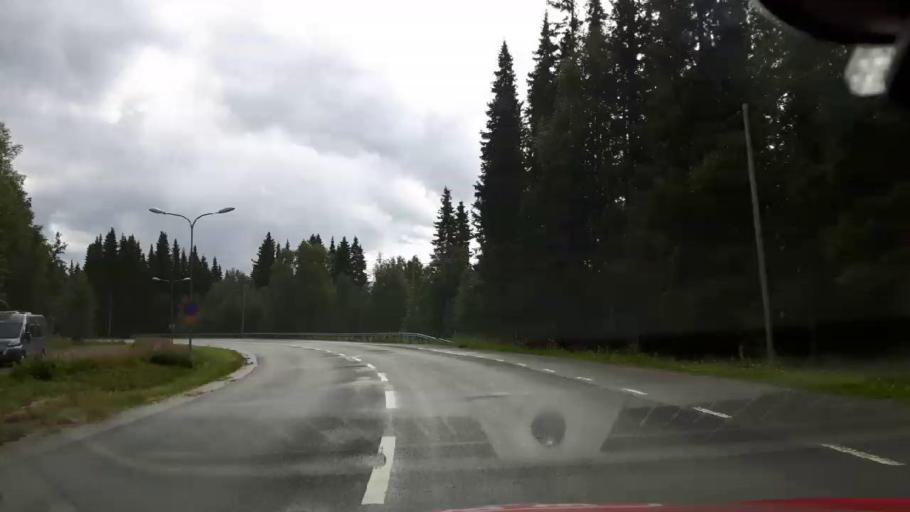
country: NO
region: Nord-Trondelag
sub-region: Lierne
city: Sandvika
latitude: 64.4942
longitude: 14.1487
